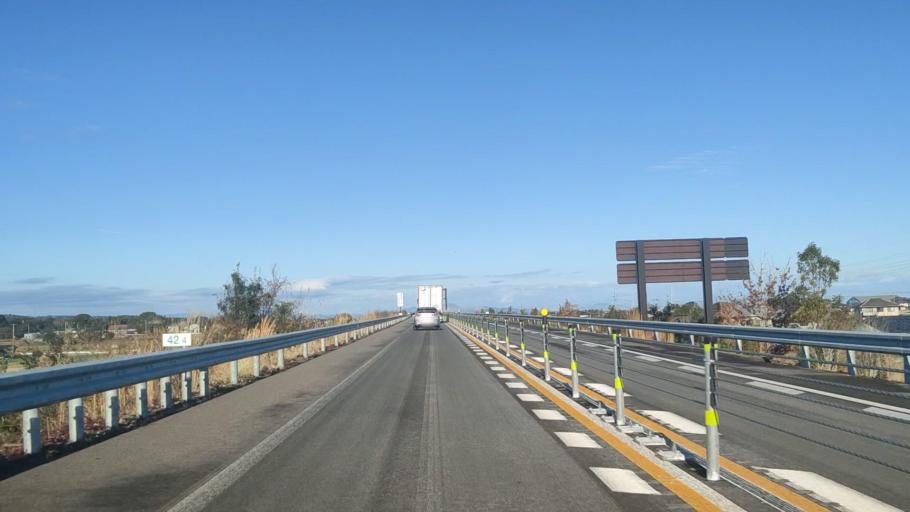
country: JP
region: Fukuoka
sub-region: Buzen-shi
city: Buzen
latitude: 33.5755
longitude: 131.1434
